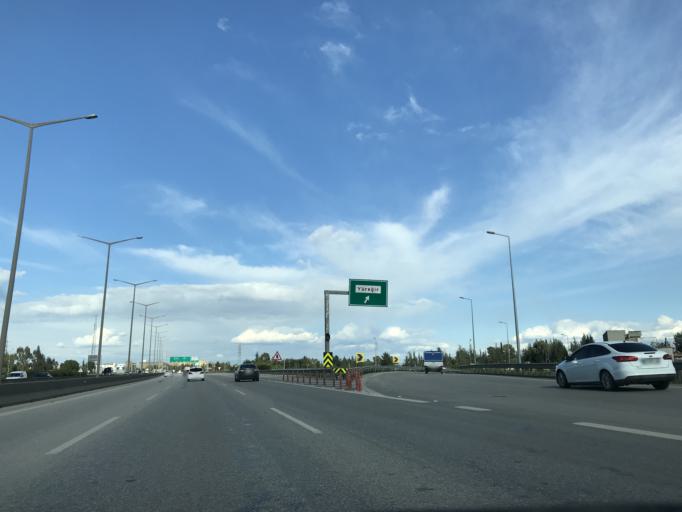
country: TR
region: Adana
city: Adana
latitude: 37.0231
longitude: 35.3393
